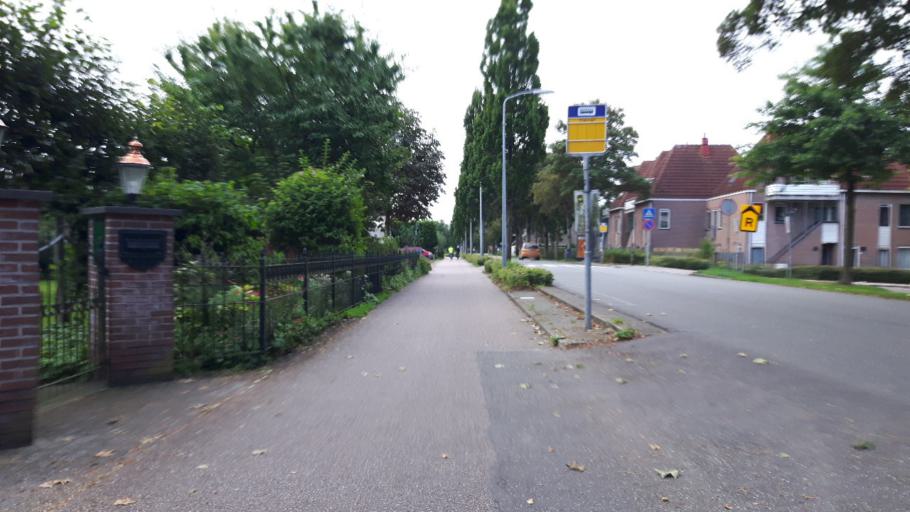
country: NL
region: North Holland
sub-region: Gemeente Hoorn
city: Hoorn
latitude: 52.6659
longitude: 5.0399
